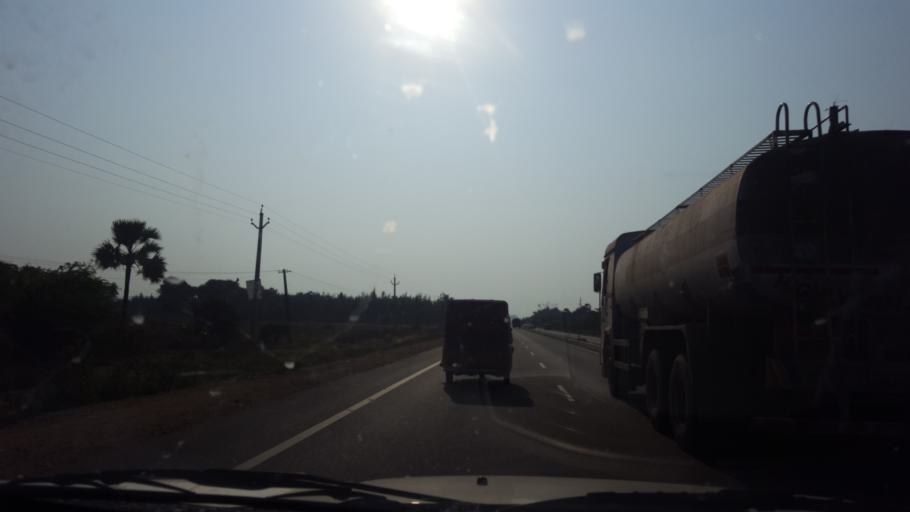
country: IN
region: Andhra Pradesh
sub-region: Vishakhapatnam
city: Etikoppaka
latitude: 17.4037
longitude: 82.6973
